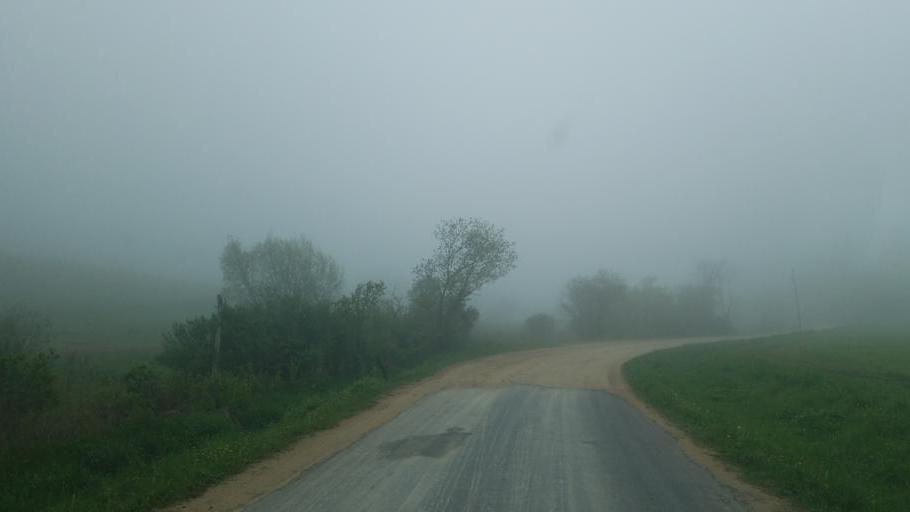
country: US
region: Wisconsin
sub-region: Vernon County
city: Hillsboro
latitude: 43.6318
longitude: -90.3496
